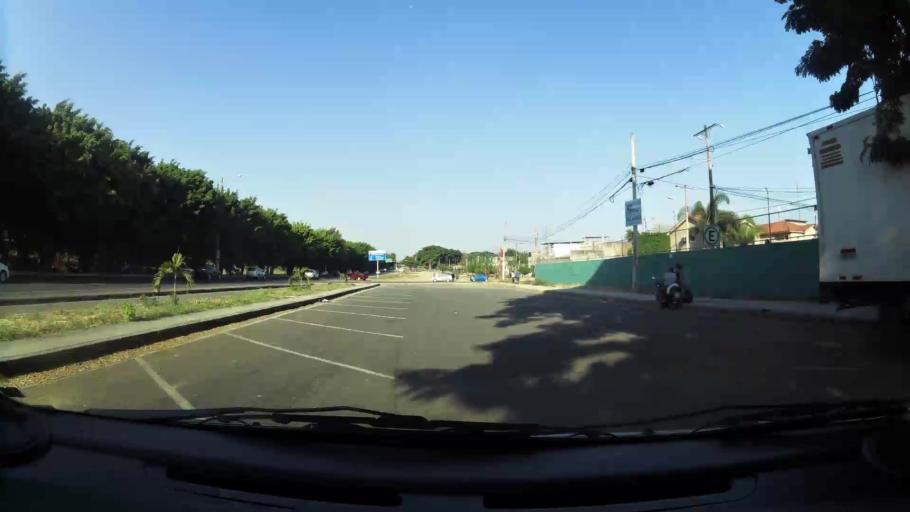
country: EC
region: Guayas
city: Santa Lucia
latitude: -2.1871
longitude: -79.9617
